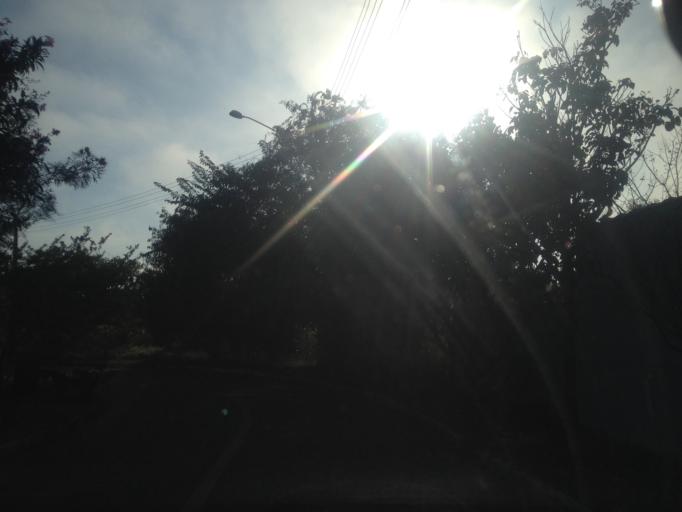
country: BR
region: Rio de Janeiro
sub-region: Porto Real
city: Porto Real
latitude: -22.4103
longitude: -44.3135
